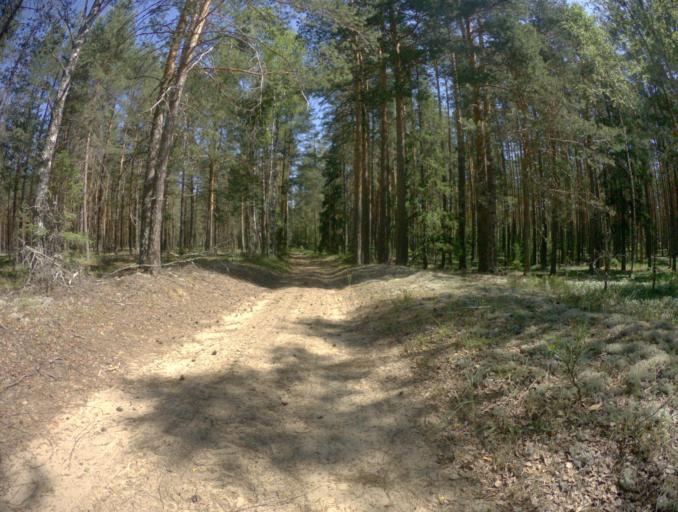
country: RU
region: Ivanovo
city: Talitsy
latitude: 56.3687
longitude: 42.3233
